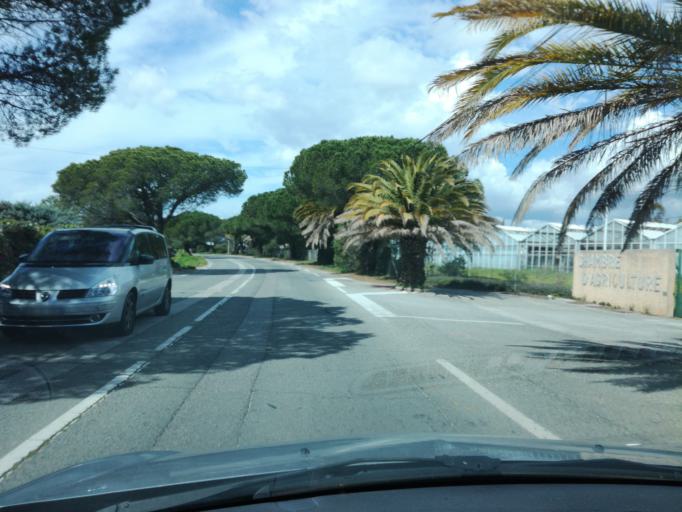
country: FR
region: Provence-Alpes-Cote d'Azur
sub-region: Departement du Var
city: Hyeres
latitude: 43.1155
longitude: 6.1533
